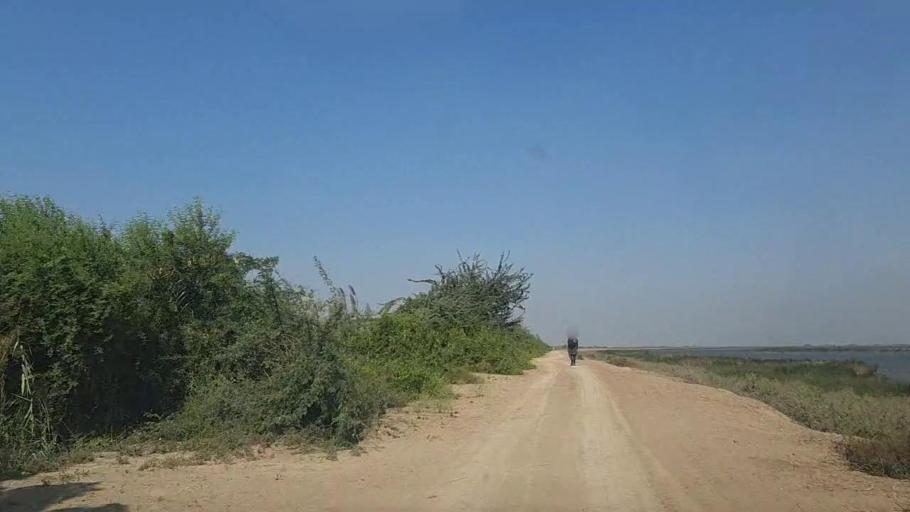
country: PK
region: Sindh
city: Daro Mehar
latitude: 24.9167
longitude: 68.0784
